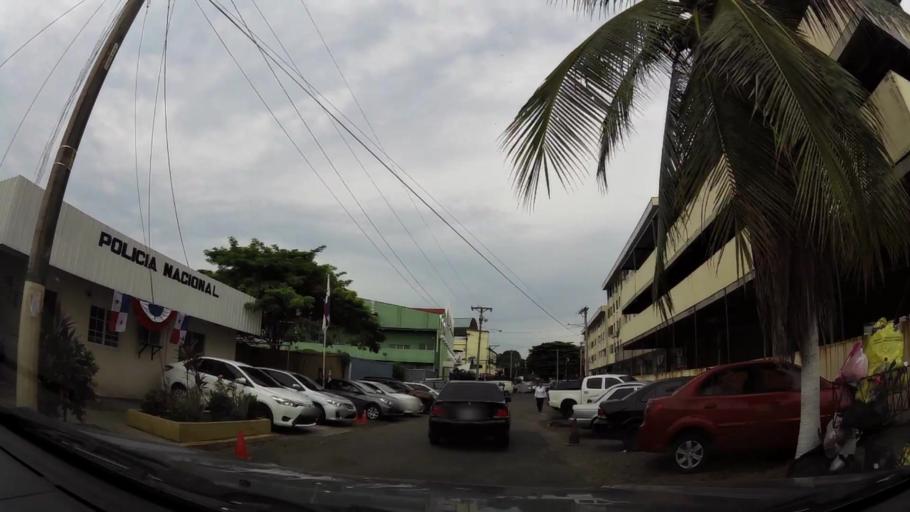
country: PA
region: Panama
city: San Miguelito
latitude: 9.0305
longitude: -79.4714
